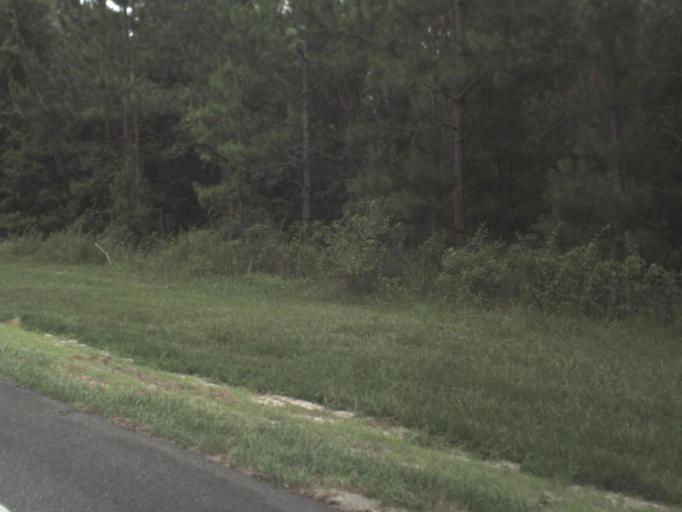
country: US
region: Florida
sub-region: Alachua County
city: Archer
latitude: 29.5402
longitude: -82.5201
